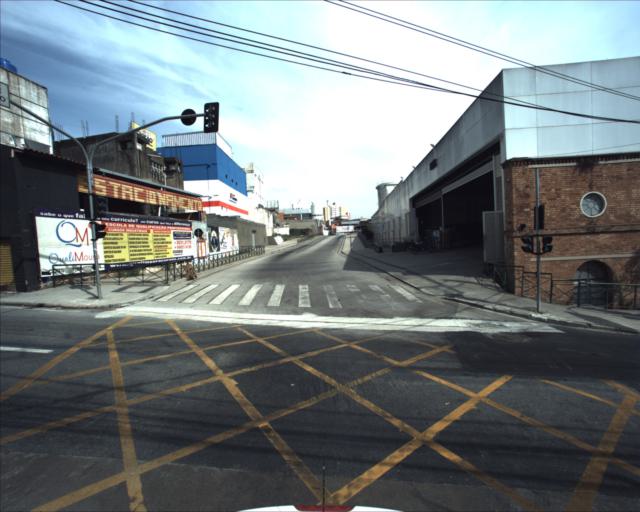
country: BR
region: Sao Paulo
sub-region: Sorocaba
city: Sorocaba
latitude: -23.4973
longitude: -47.4582
